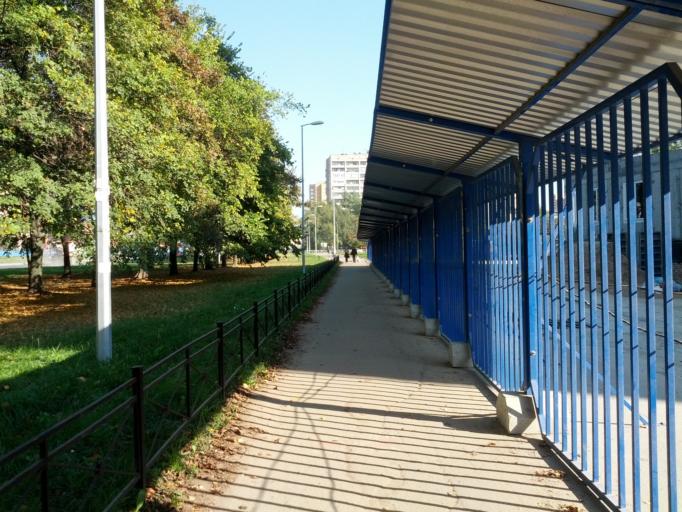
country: RU
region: St.-Petersburg
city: Kupchino
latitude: 59.8423
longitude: 30.3530
